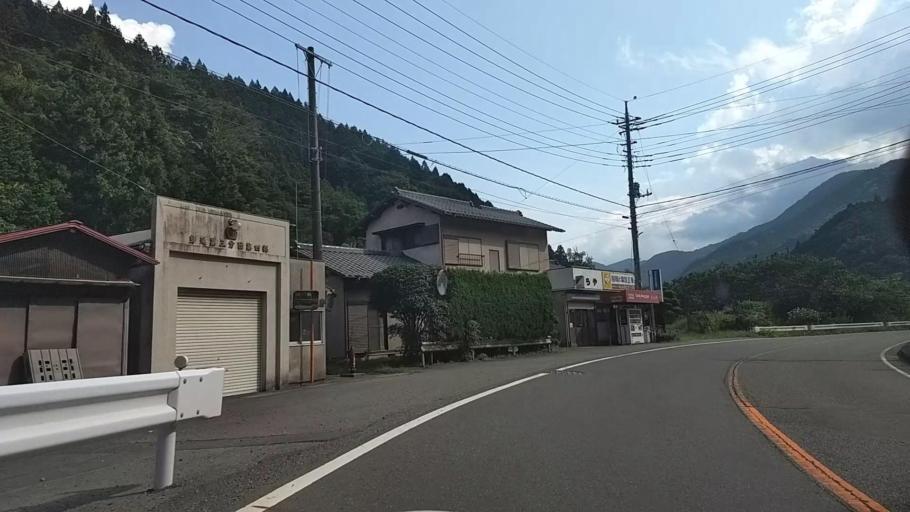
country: JP
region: Shizuoka
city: Fujinomiya
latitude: 35.3611
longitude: 138.4226
